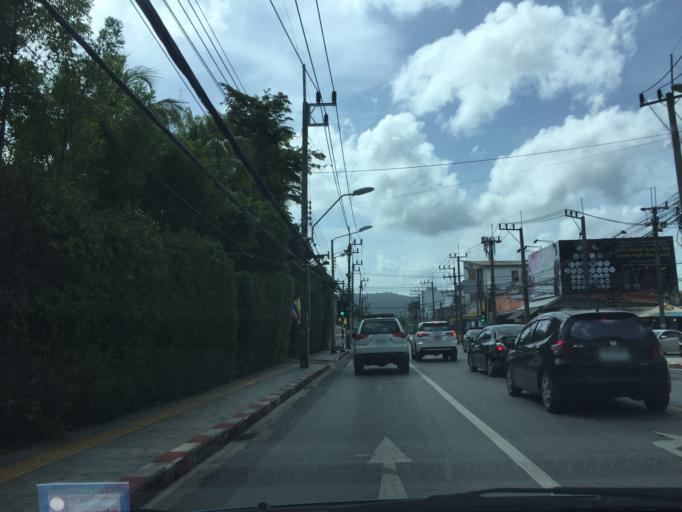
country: TH
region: Phuket
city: Wichit
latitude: 7.8954
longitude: 98.3849
